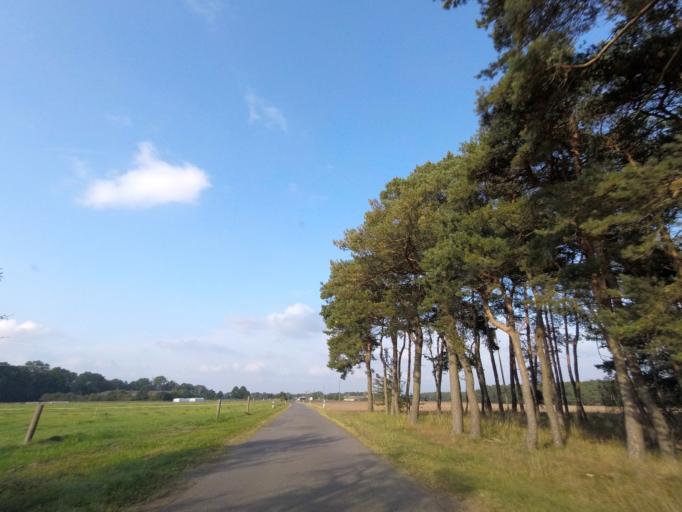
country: DE
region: Brandenburg
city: Linthe
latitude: 52.1461
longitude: 12.7227
